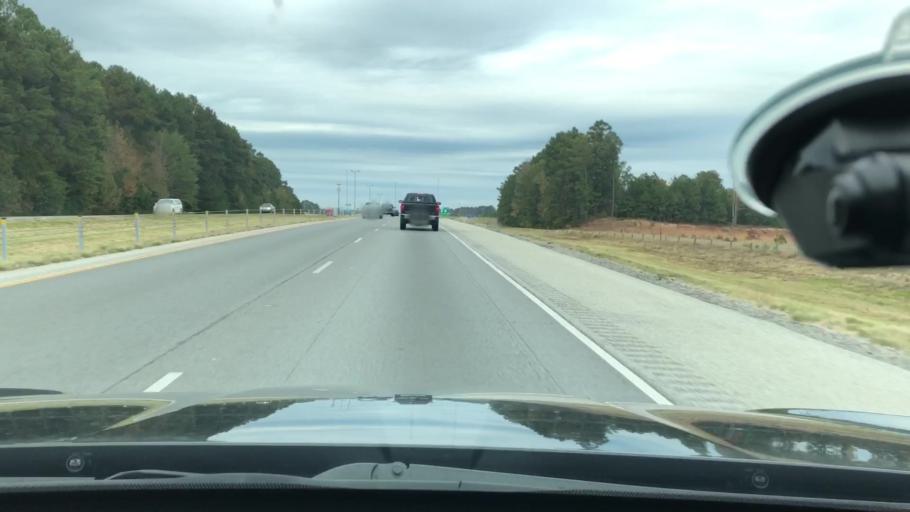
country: US
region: Arkansas
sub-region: Clark County
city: Arkadelphia
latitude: 34.1110
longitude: -93.0968
